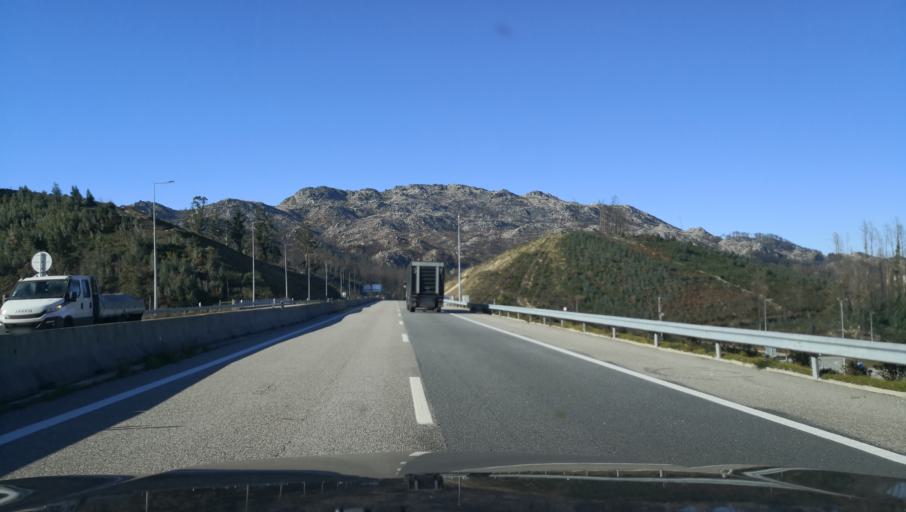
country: PT
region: Viseu
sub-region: Vouzela
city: Vouzela
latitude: 40.6497
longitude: -8.0701
